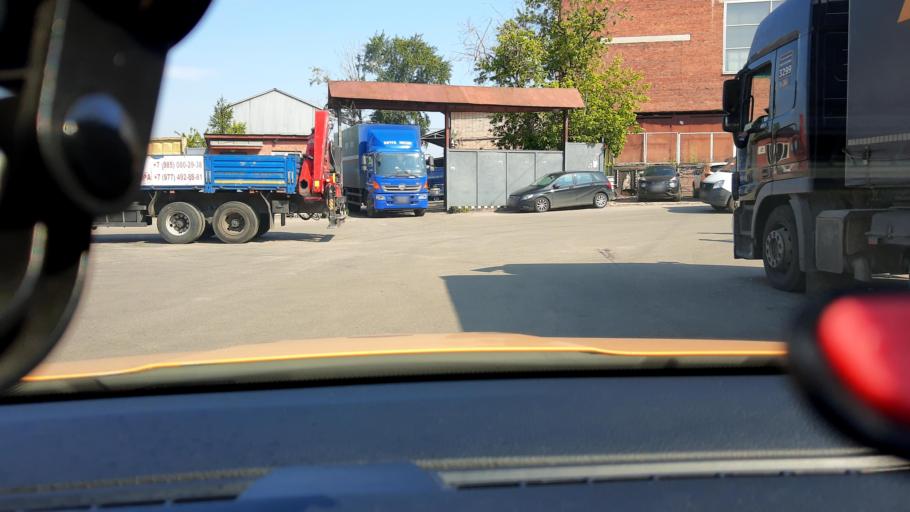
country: RU
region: Moscow
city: Sokol'niki
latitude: 55.7788
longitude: 37.6588
